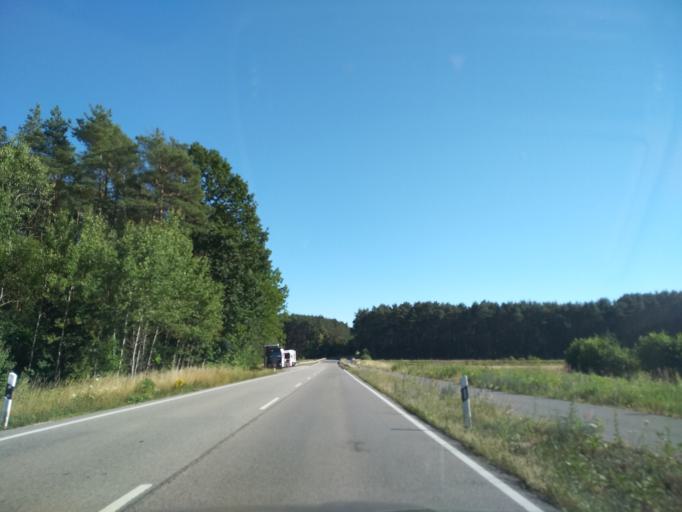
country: DE
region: Bavaria
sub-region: Regierungsbezirk Mittelfranken
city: Rottenbach
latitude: 49.6577
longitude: 10.9179
